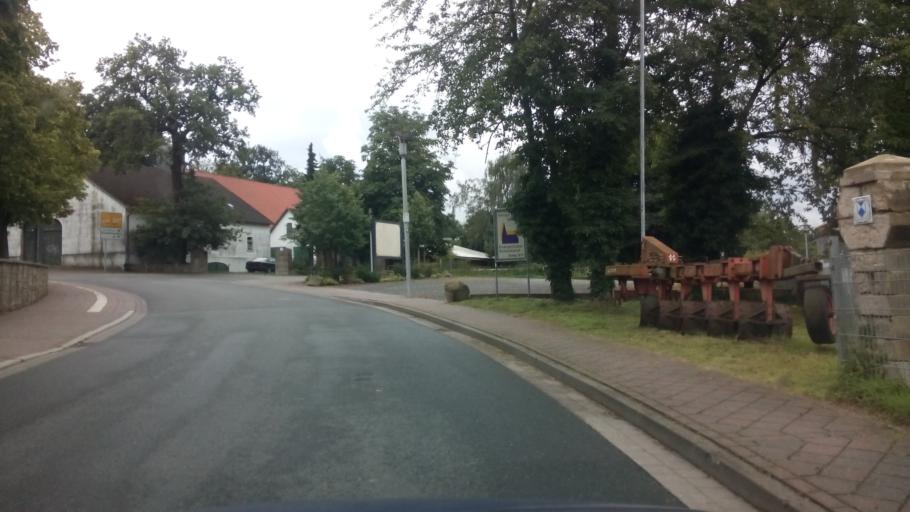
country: DE
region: Lower Saxony
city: Bohmte
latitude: 52.3670
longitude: 8.3114
